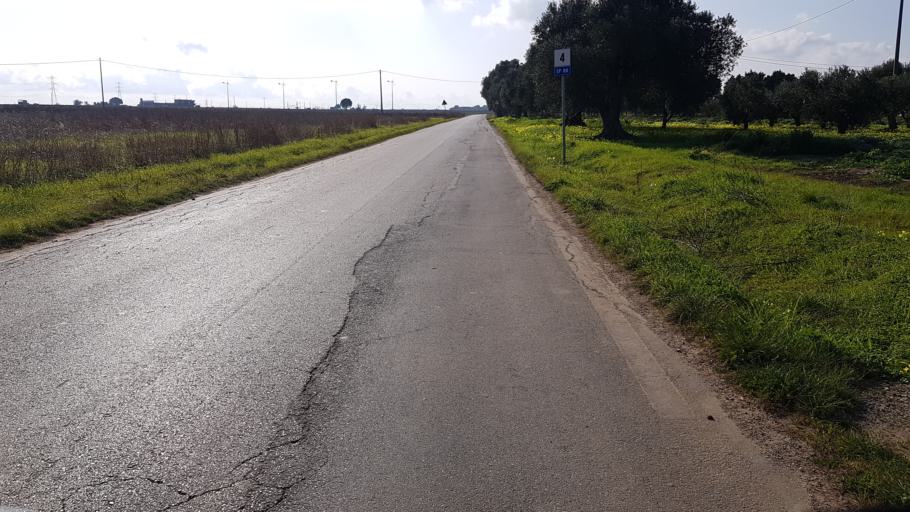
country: IT
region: Apulia
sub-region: Provincia di Brindisi
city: La Rosa
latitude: 40.5808
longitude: 17.9020
